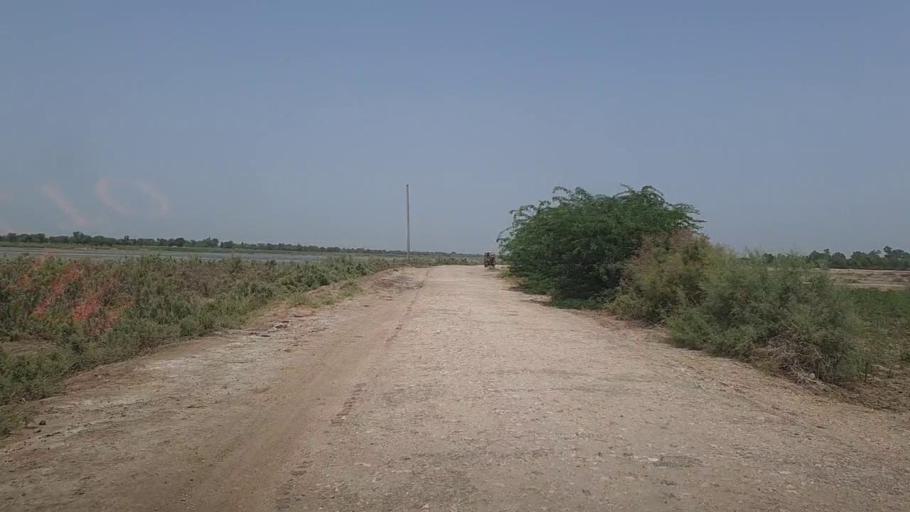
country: PK
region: Sindh
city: Pad Idan
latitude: 26.8528
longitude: 68.2954
